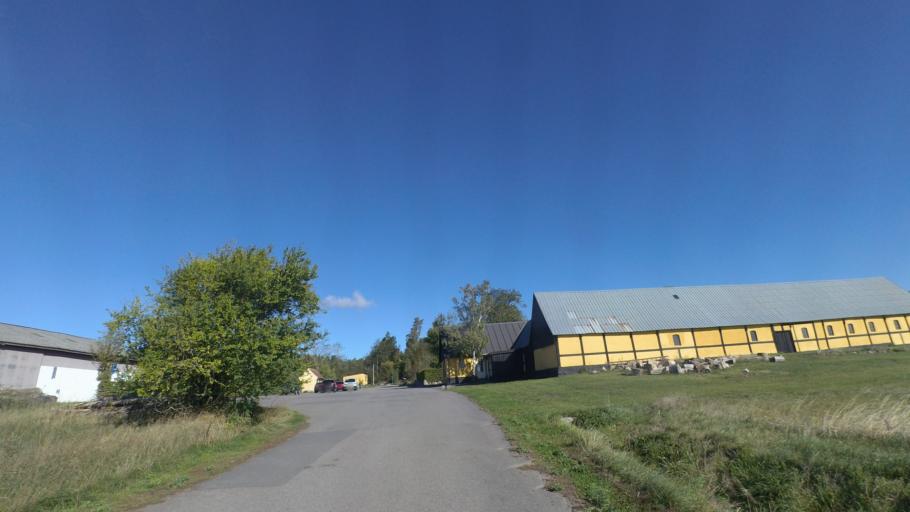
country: DK
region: Capital Region
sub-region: Bornholm Kommune
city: Nexo
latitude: 55.0797
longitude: 15.1010
